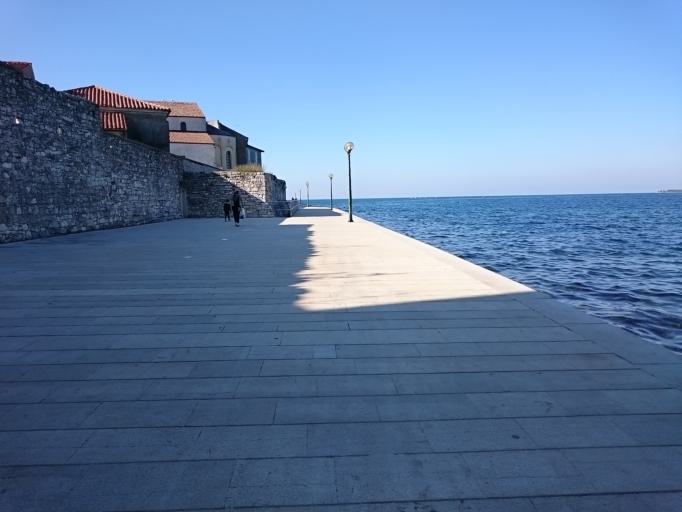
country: HR
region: Istarska
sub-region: Grad Porec
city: Porec
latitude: 45.2287
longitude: 13.5942
